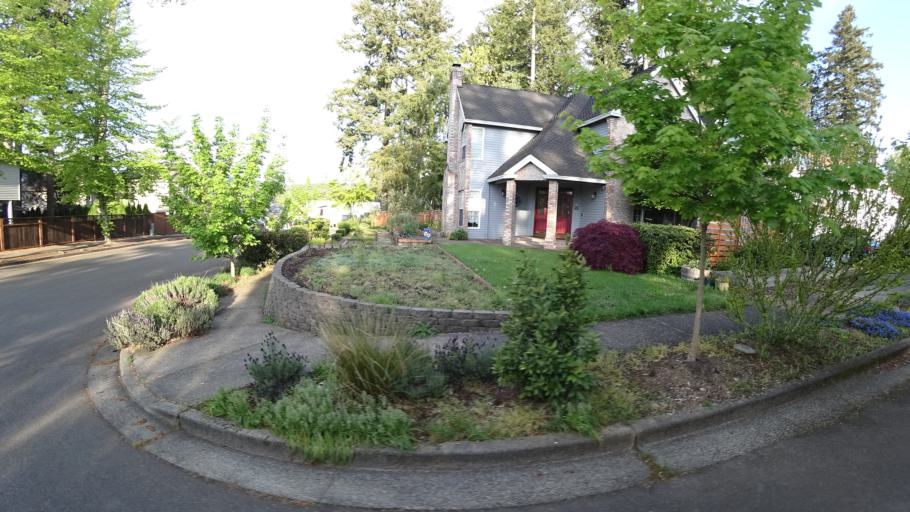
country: US
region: Oregon
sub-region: Washington County
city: Beaverton
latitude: 45.4477
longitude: -122.8230
